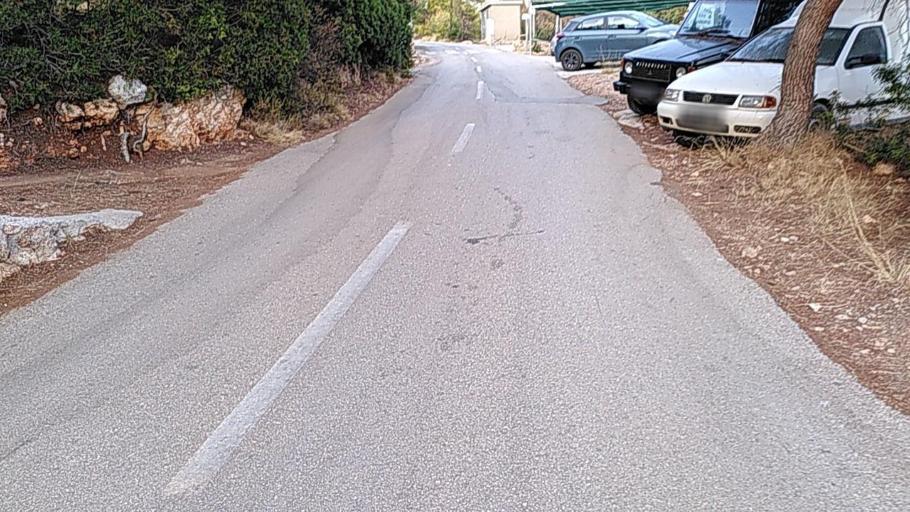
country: HR
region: Splitsko-Dalmatinska
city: Stari Grad
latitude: 43.1348
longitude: 16.5876
